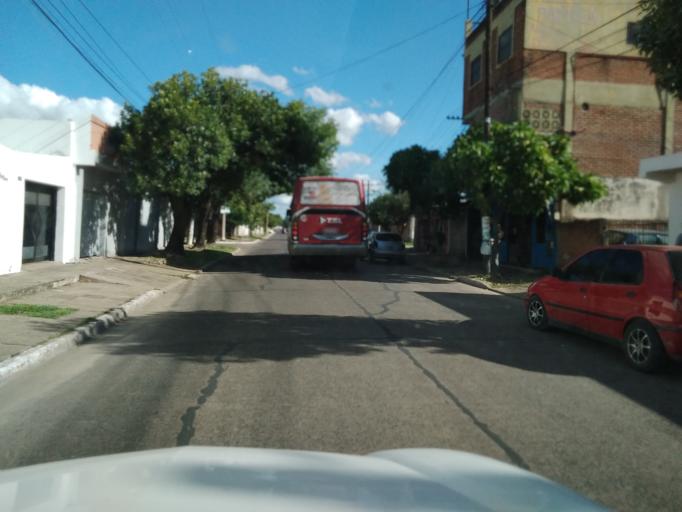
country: AR
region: Corrientes
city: Corrientes
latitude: -27.4916
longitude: -58.8332
